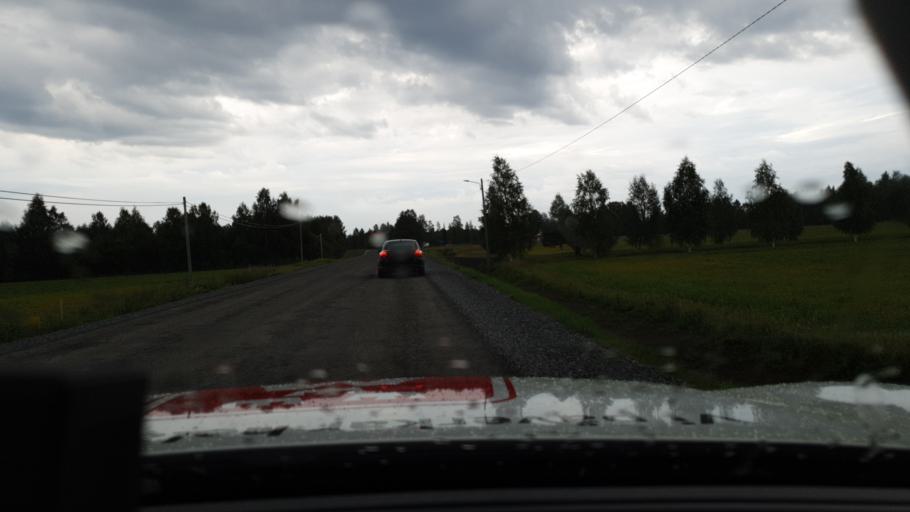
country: SE
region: Norrbotten
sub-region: Bodens Kommun
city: Boden
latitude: 65.8549
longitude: 21.4805
